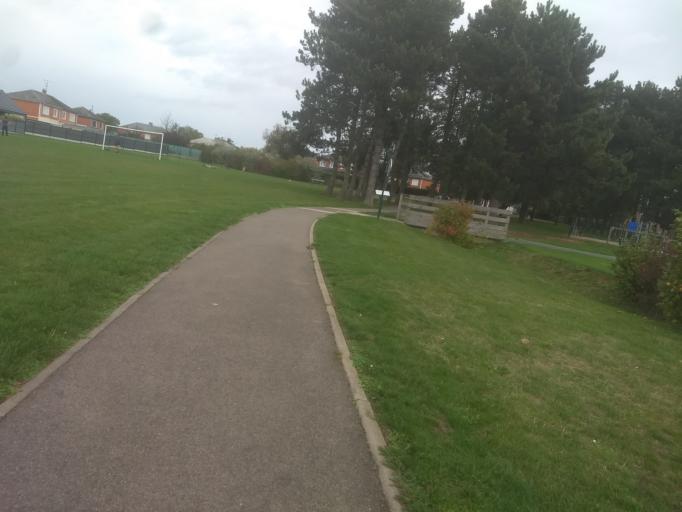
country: FR
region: Nord-Pas-de-Calais
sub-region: Departement du Pas-de-Calais
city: Beaurains
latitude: 50.2623
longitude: 2.7784
